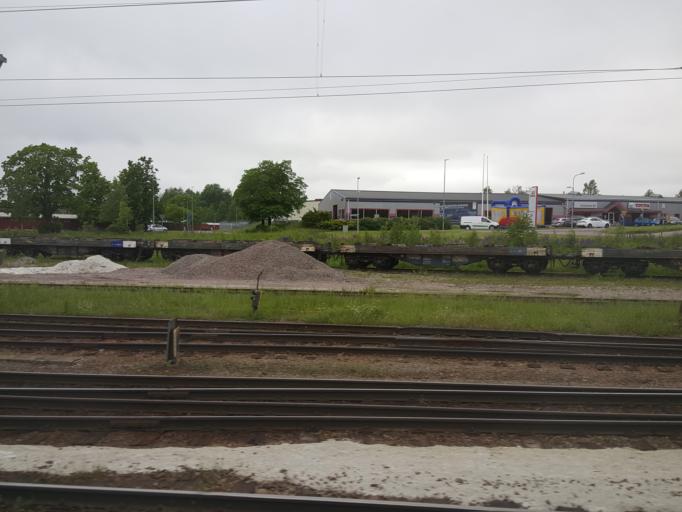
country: SE
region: Dalarna
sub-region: Avesta Kommun
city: Avesta
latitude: 60.1328
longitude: 16.2143
